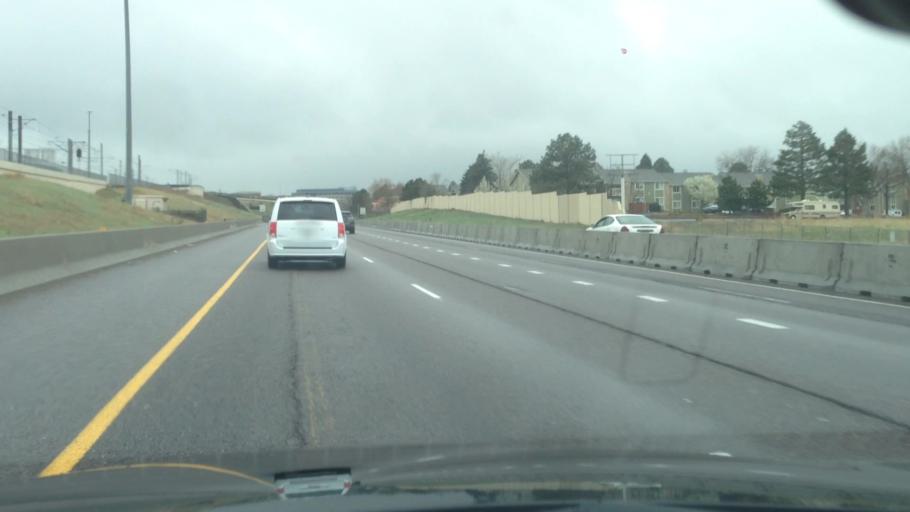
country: US
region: Colorado
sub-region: Arapahoe County
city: Castlewood
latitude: 39.6353
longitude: -104.8977
